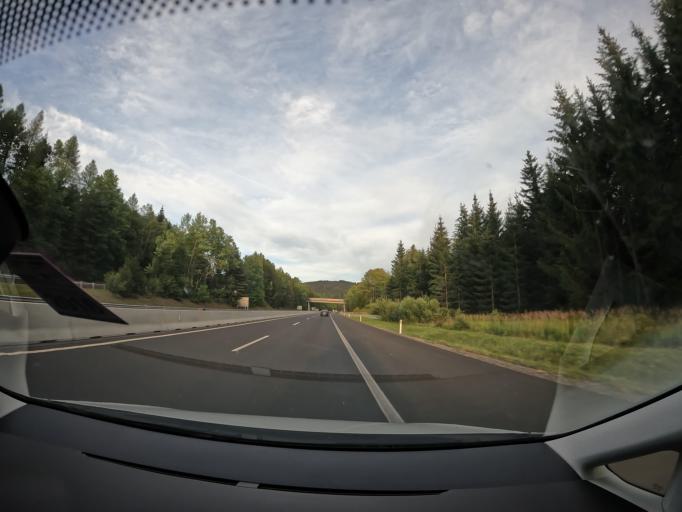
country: AT
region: Carinthia
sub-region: Politischer Bezirk Wolfsberg
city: Preitenegg
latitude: 46.9656
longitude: 14.9499
